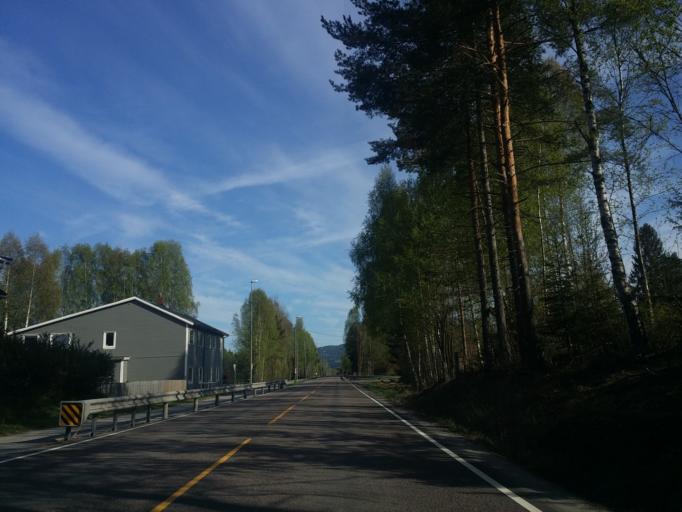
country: NO
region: Telemark
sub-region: Notodden
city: Notodden
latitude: 59.5909
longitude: 9.1527
